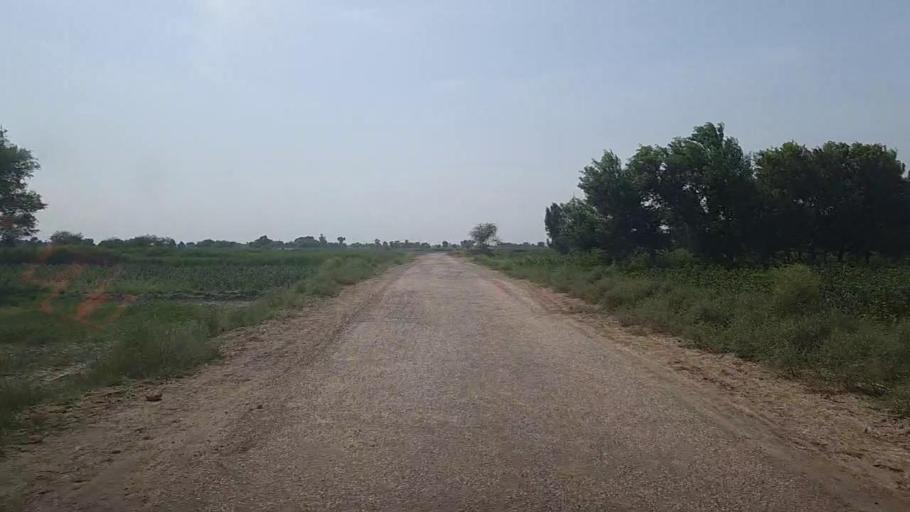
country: PK
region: Sindh
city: Ubauro
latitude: 28.1388
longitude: 69.8174
